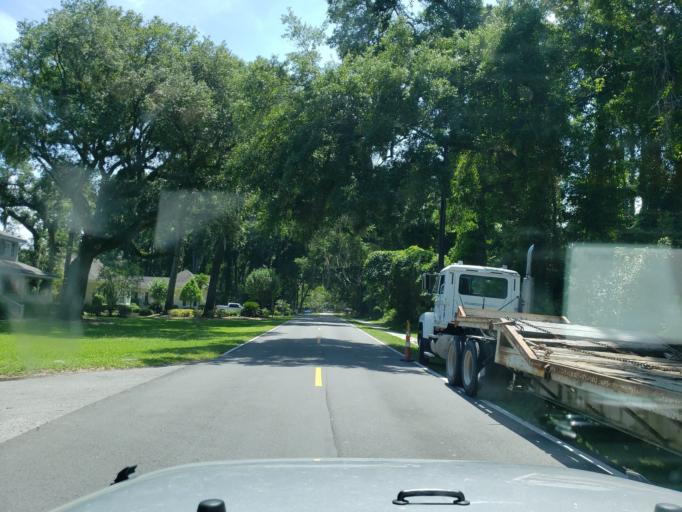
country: US
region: Georgia
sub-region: Chatham County
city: Whitemarsh Island
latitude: 32.0215
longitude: -81.0138
